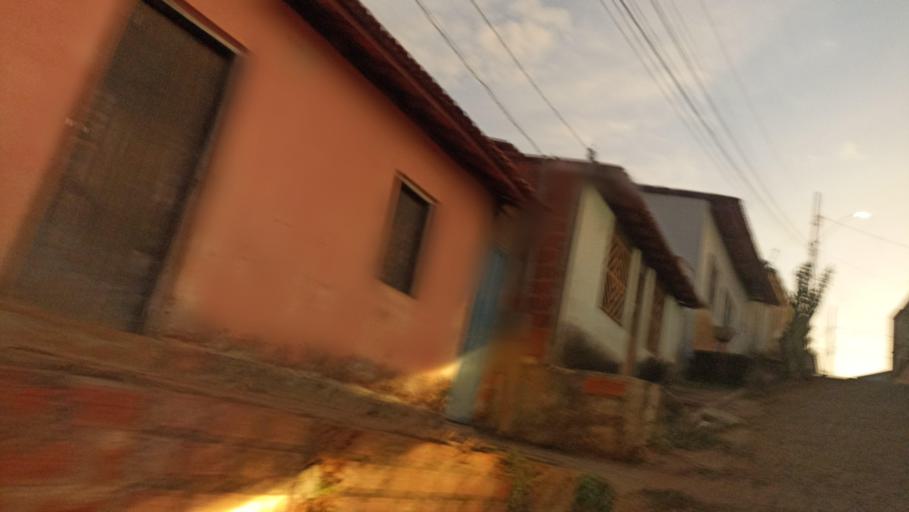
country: BR
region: Minas Gerais
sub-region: Aracuai
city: Aracuai
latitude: -16.6186
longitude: -42.1808
